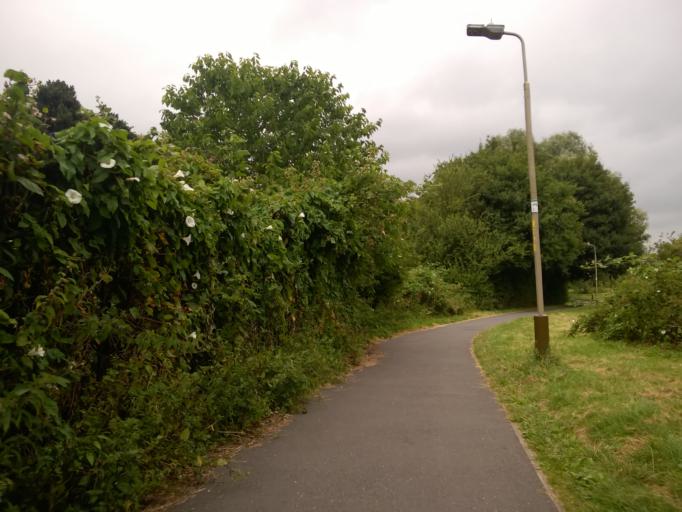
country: GB
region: England
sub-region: City of Leicester
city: Leicester
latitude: 52.6545
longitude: -1.1300
